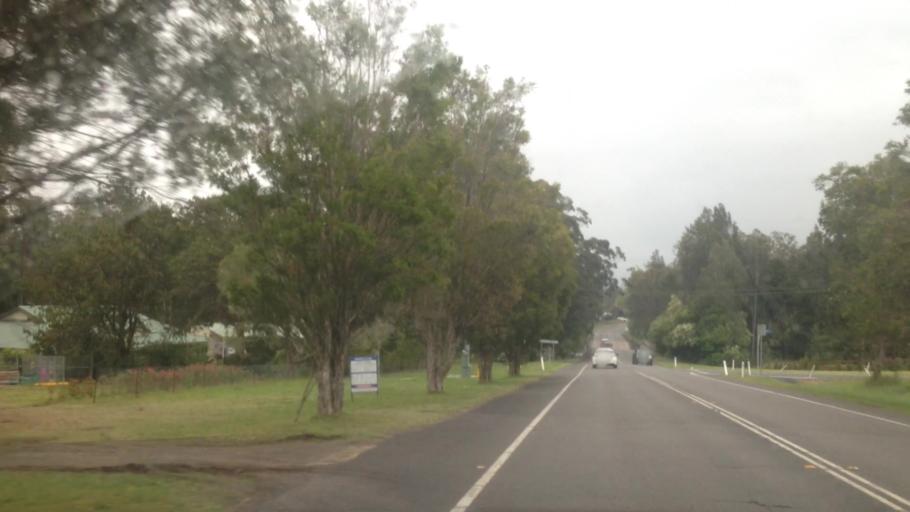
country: AU
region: New South Wales
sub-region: Lake Macquarie Shire
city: Dora Creek
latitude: -33.1018
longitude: 151.4760
